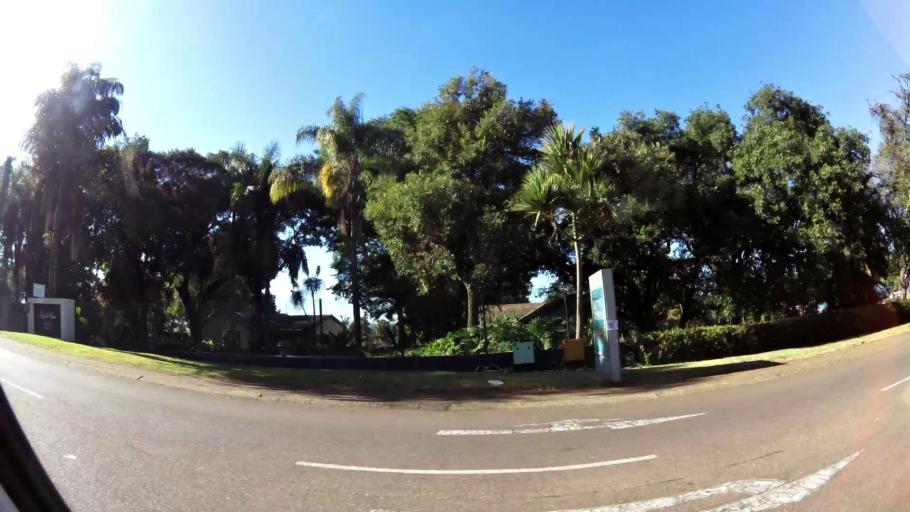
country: ZA
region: Limpopo
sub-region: Mopani District Municipality
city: Tzaneen
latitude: -23.8375
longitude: 30.1538
